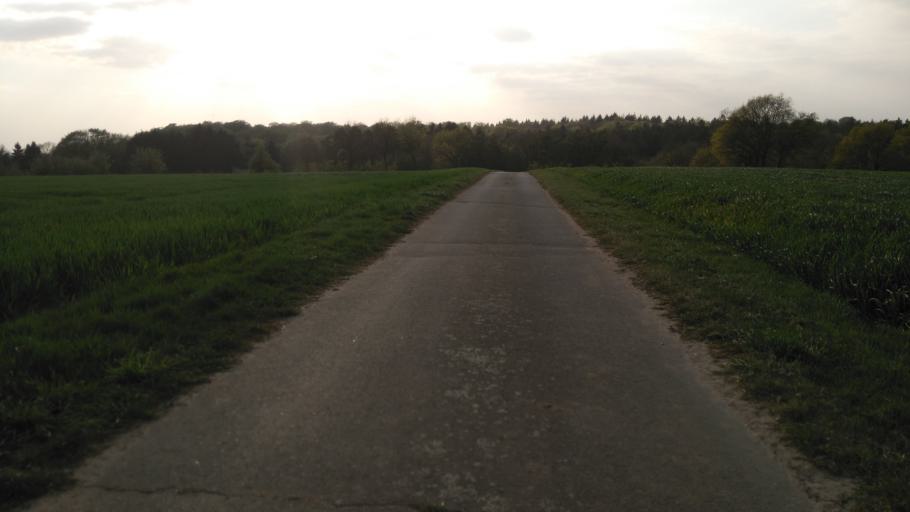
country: DE
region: Lower Saxony
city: Nottensdorf
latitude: 53.4708
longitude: 9.6288
